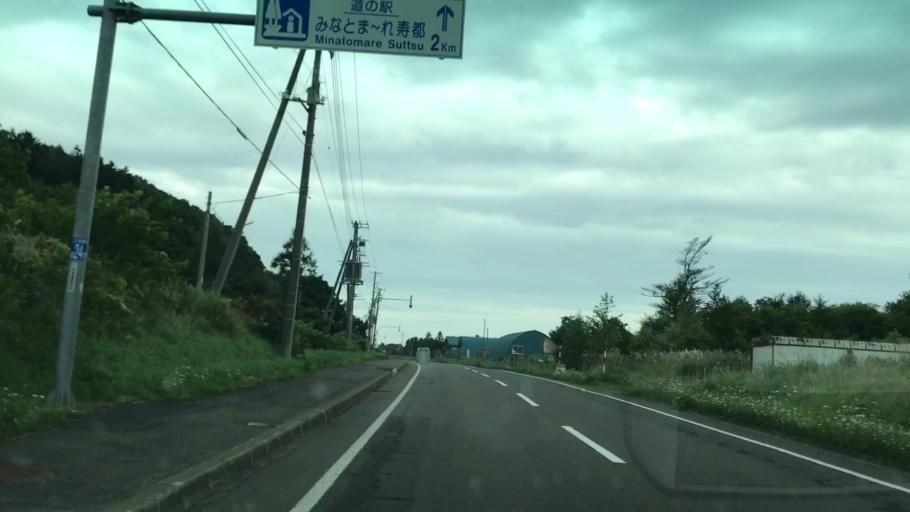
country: JP
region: Hokkaido
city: Iwanai
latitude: 42.7793
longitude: 140.2379
